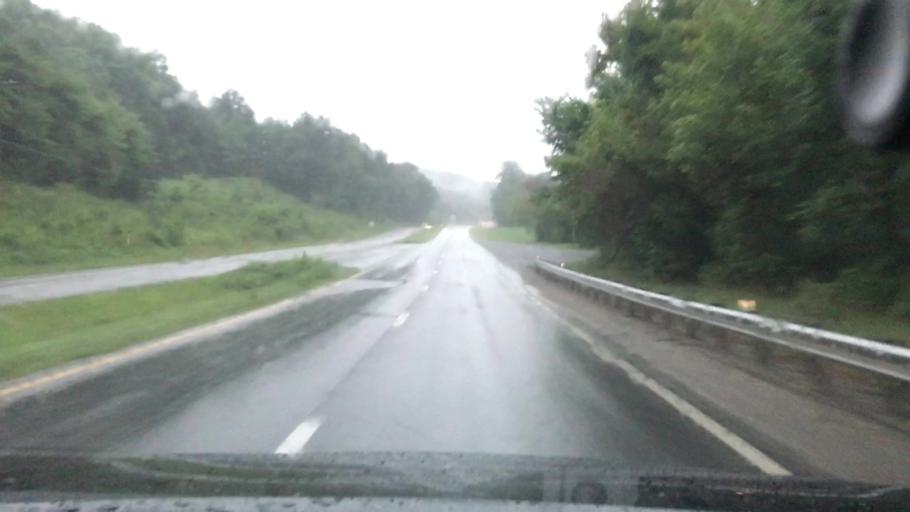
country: US
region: Virginia
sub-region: Giles County
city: Narrows
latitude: 37.3495
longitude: -80.7751
